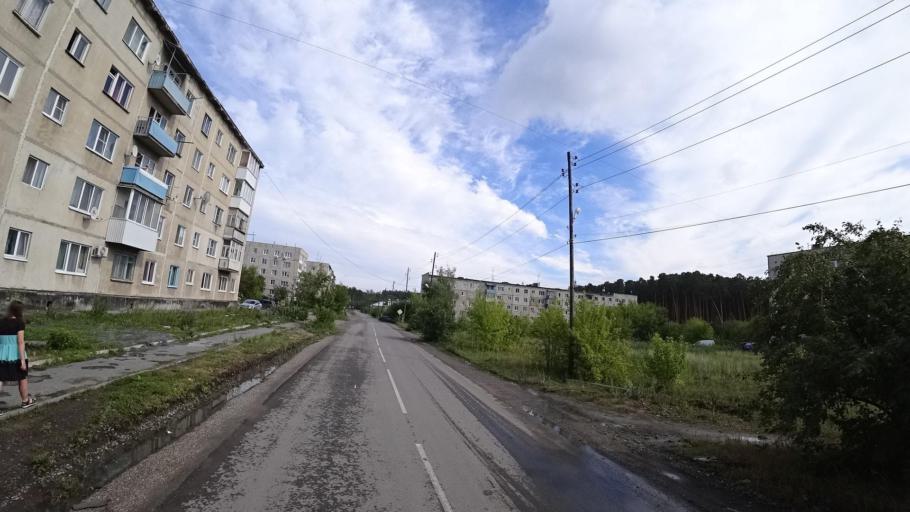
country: RU
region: Sverdlovsk
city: Kamyshlov
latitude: 56.8371
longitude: 62.7286
